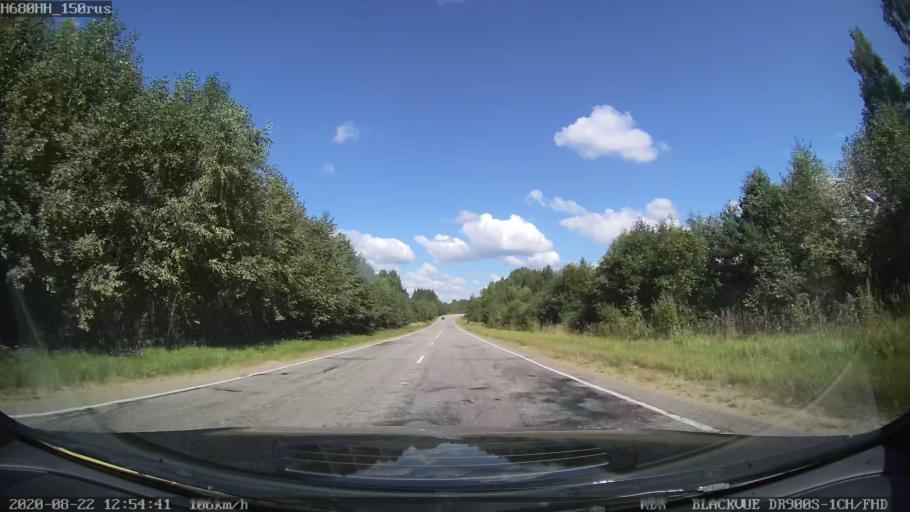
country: RU
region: Tverskaya
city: Rameshki
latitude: 57.5347
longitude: 36.2884
